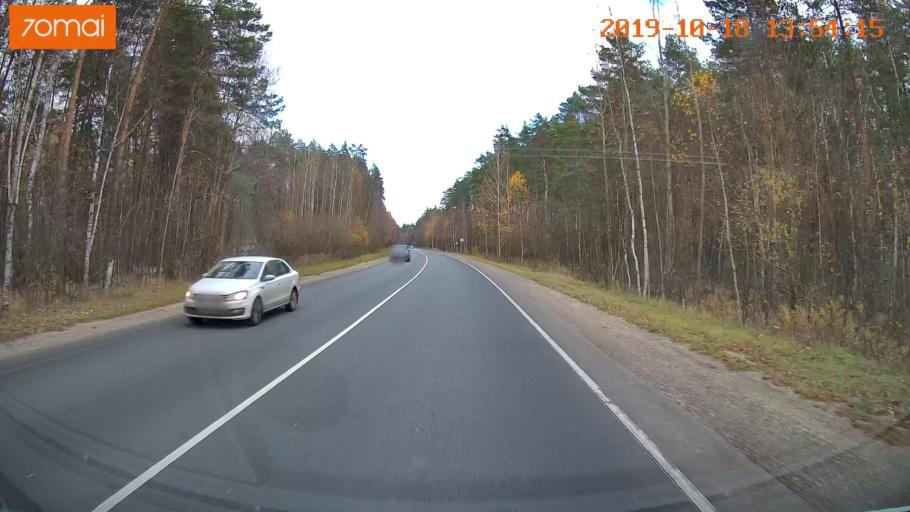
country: RU
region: Rjazan
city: Spas-Klepiki
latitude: 55.0404
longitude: 40.0044
